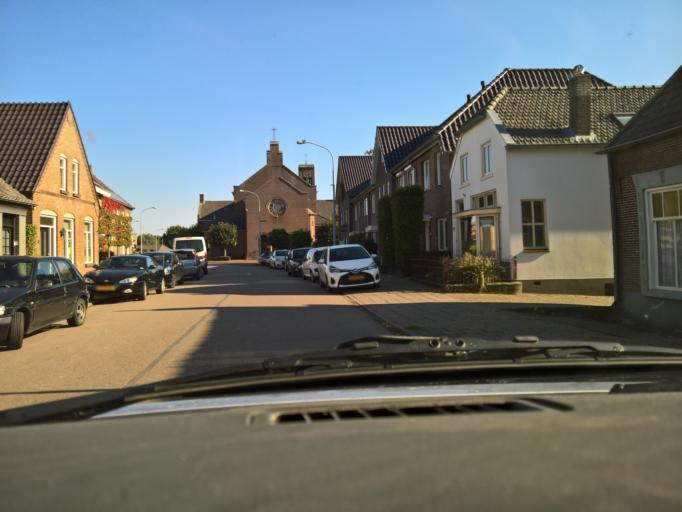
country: NL
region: Gelderland
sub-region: Gemeente Tiel
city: Tiel
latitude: 51.8809
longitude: 5.4665
